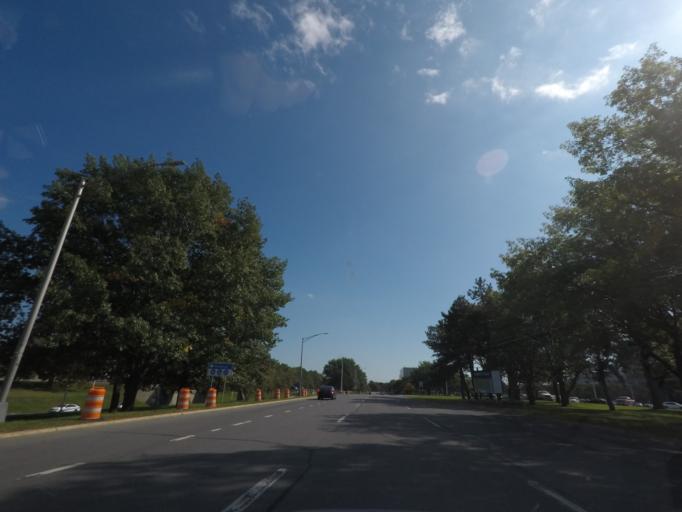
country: US
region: New York
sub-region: Albany County
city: Roessleville
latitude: 42.6825
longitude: -73.8088
